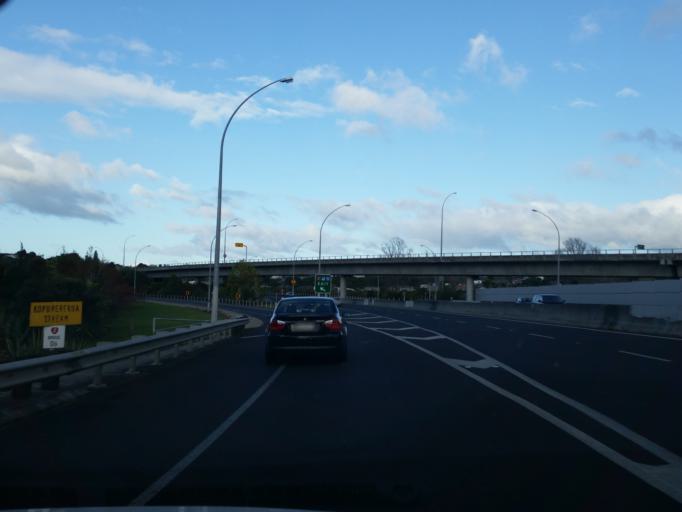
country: NZ
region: Bay of Plenty
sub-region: Tauranga City
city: Tauranga
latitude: -37.7023
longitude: 176.1395
